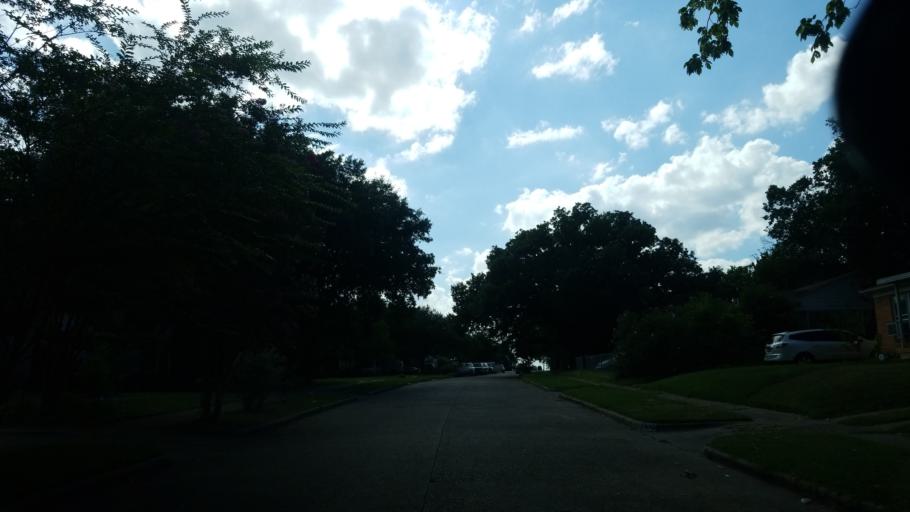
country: US
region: Texas
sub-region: Dallas County
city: Balch Springs
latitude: 32.7731
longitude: -96.7090
